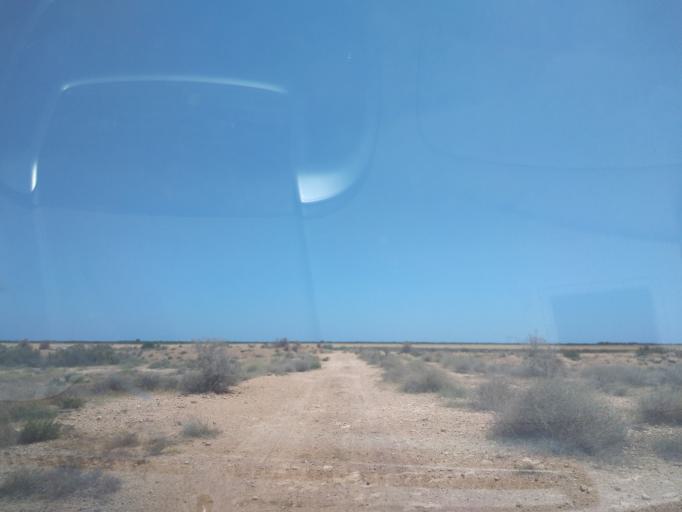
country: TN
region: Susah
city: Harqalah
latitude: 36.1701
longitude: 10.4468
